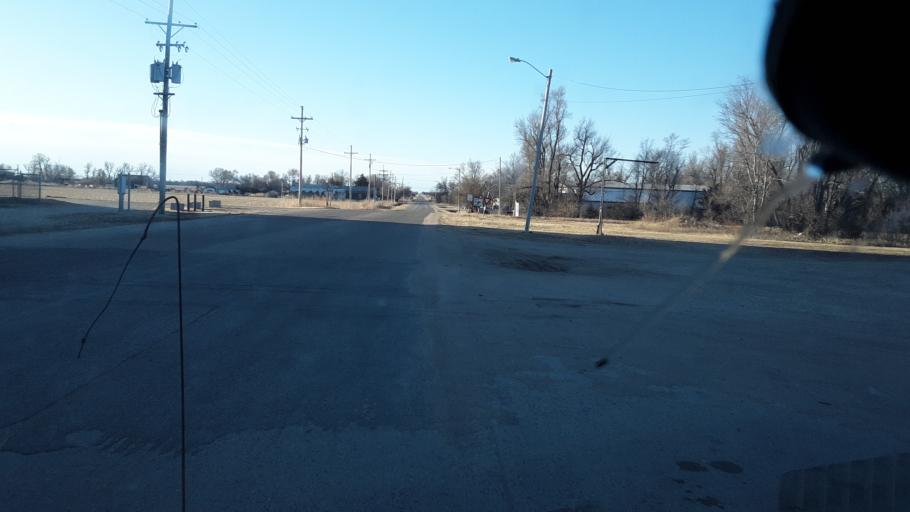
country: US
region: Kansas
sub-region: Rice County
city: Lyons
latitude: 38.3524
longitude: -98.3495
